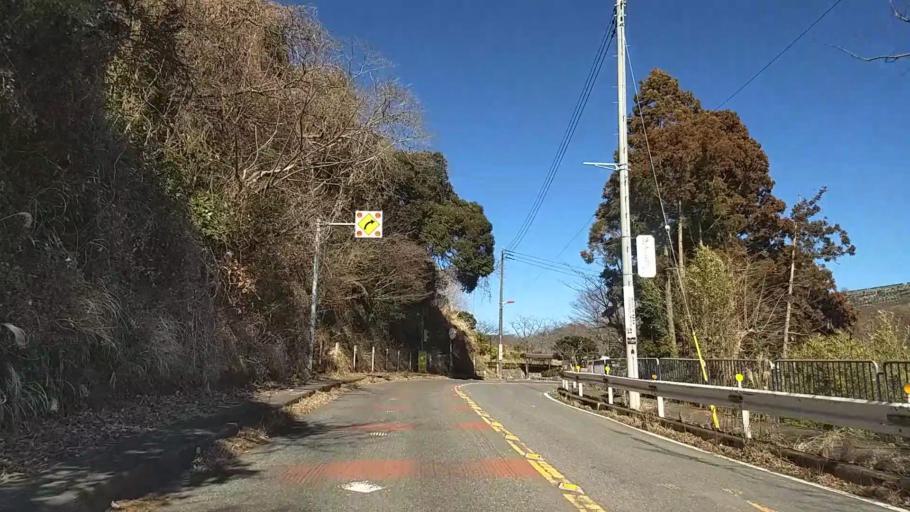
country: JP
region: Kanagawa
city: Zushi
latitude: 35.3253
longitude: 139.5818
